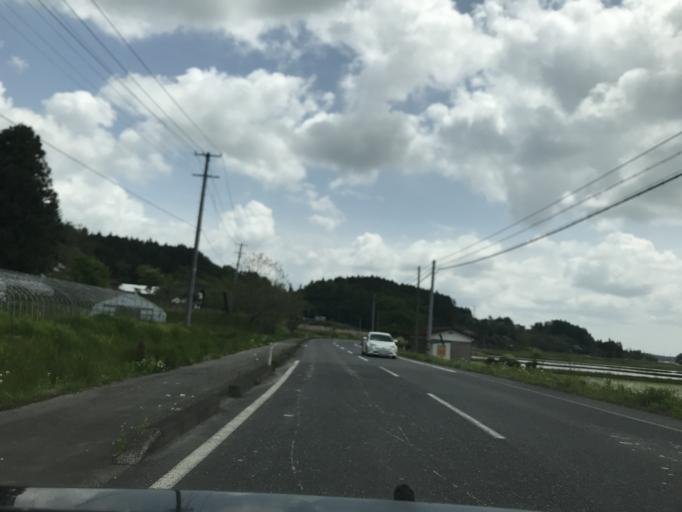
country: JP
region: Miyagi
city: Furukawa
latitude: 38.6924
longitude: 140.9332
